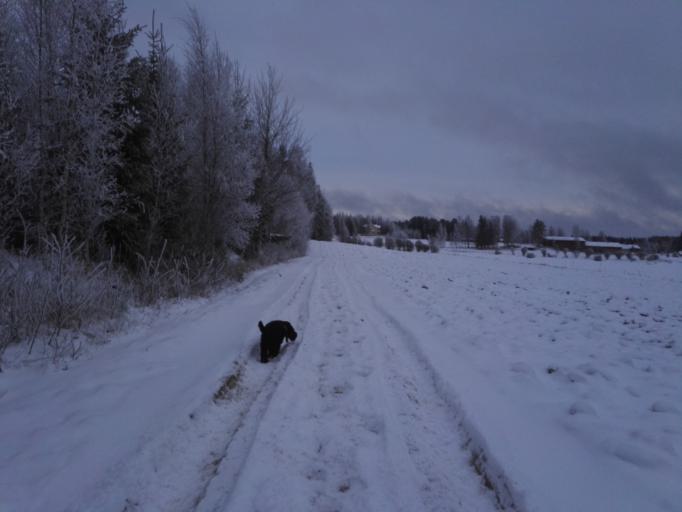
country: FI
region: Satakunta
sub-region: Pohjois-Satakunta
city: Jaemijaervi
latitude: 61.7847
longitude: 22.8730
